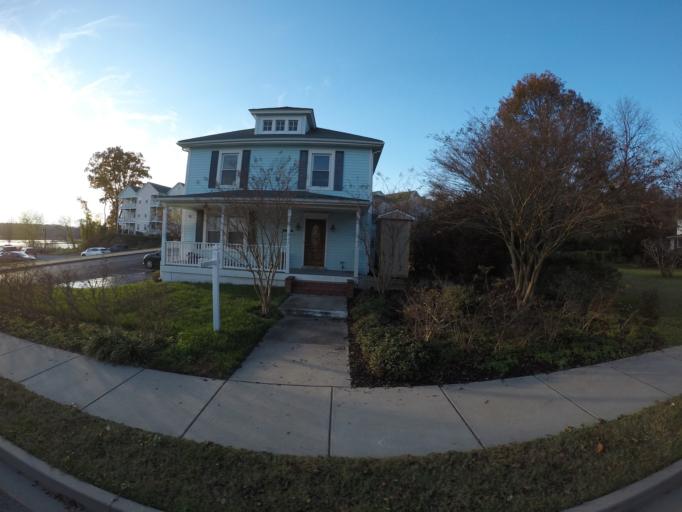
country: US
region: Maryland
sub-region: Saint Mary's County
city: Leonardtown
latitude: 38.2870
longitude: -76.6381
